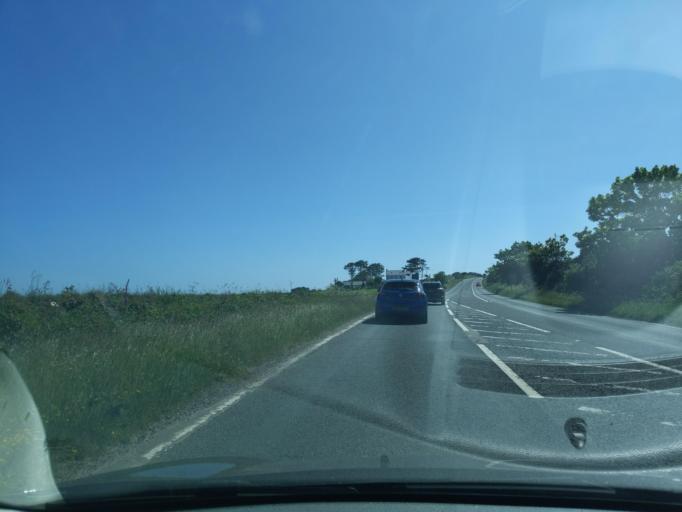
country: GB
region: England
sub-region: Cornwall
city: Wendron
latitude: 50.1459
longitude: -5.2126
